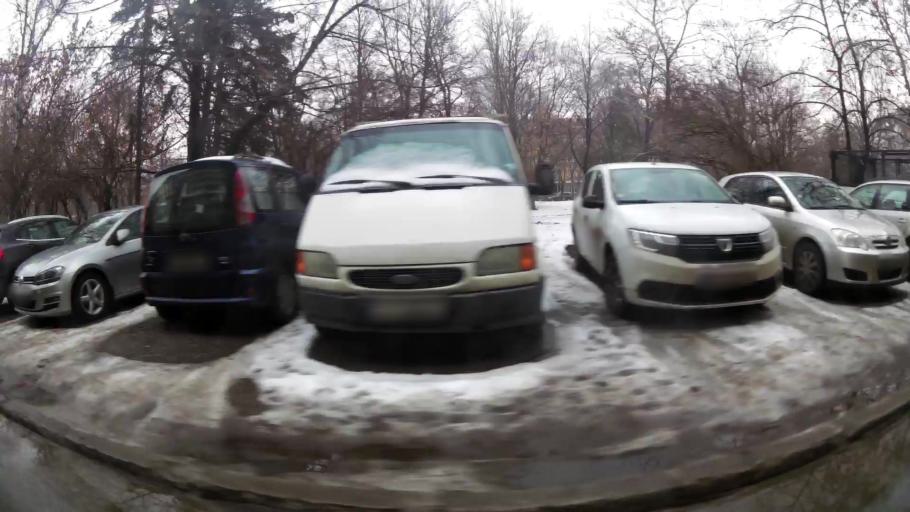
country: BG
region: Sofia-Capital
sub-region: Stolichna Obshtina
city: Sofia
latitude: 42.6790
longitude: 23.2977
